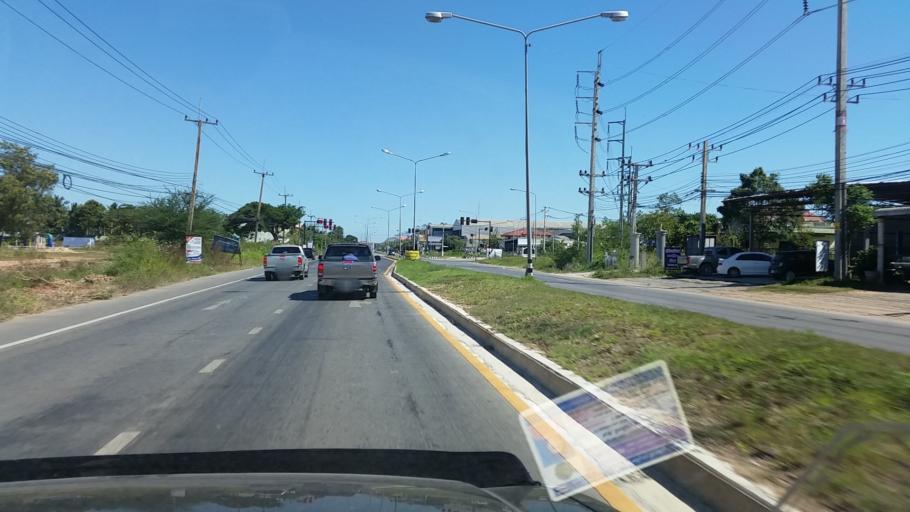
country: TH
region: Chaiyaphum
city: Chaiyaphum
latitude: 15.7938
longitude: 102.0059
